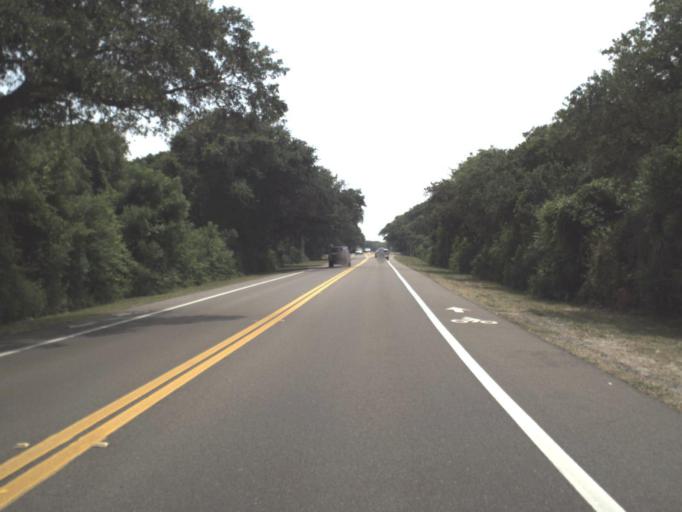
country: US
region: Florida
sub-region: Nassau County
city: Fernandina Beach
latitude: 30.5400
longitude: -81.4430
